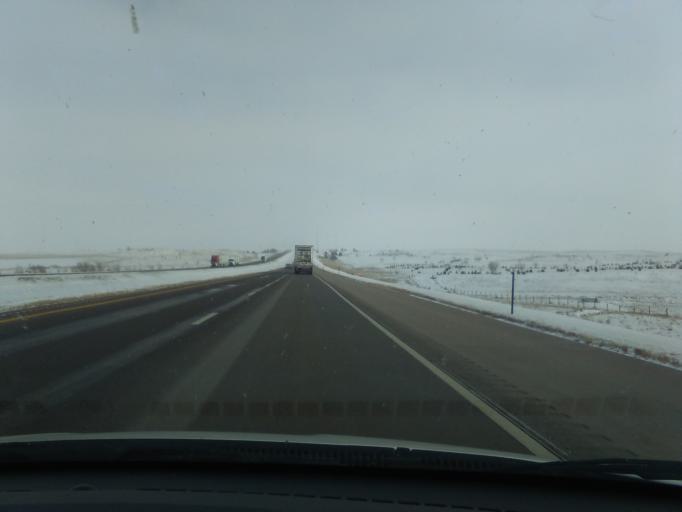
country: US
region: Nebraska
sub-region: Kimball County
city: Kimball
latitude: 41.2185
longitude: -103.6426
